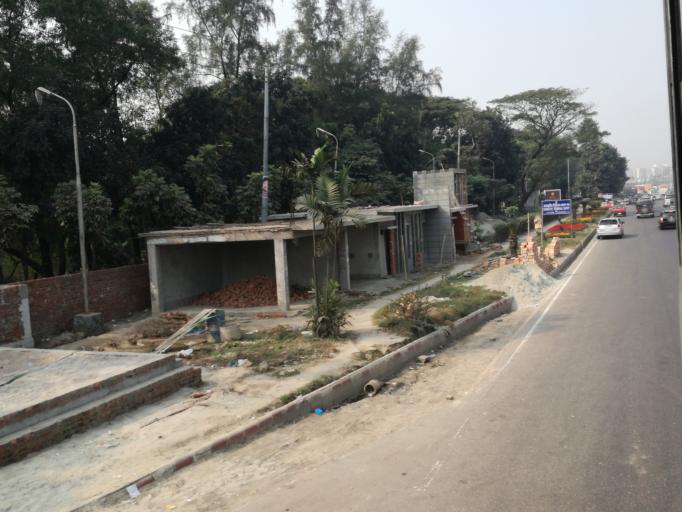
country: BD
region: Dhaka
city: Tungi
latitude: 23.8463
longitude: 90.4118
